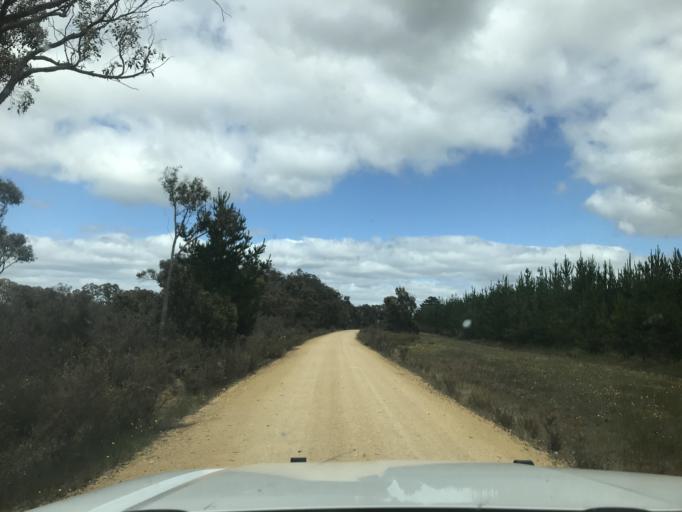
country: AU
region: South Australia
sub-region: Wattle Range
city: Penola
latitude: -37.3185
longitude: 141.1420
